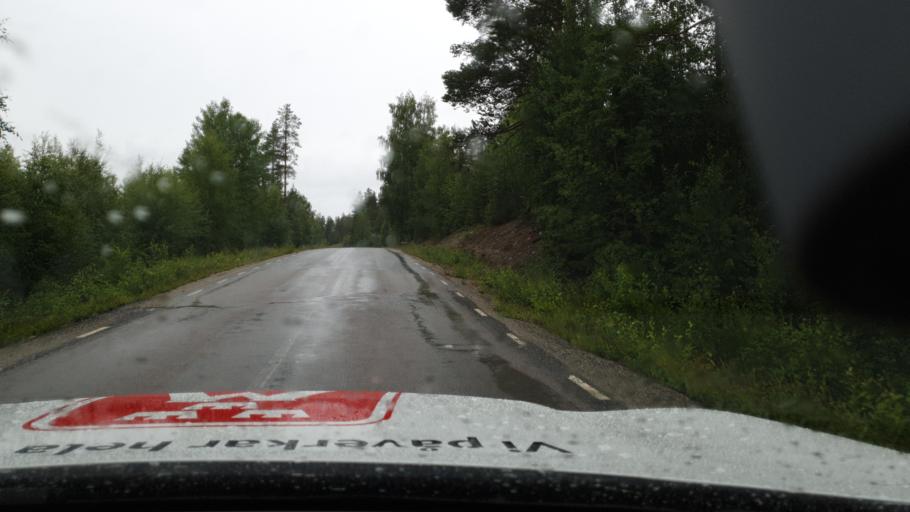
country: SE
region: Vaesterbotten
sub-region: Vindelns Kommun
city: Vindeln
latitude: 64.4976
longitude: 19.8010
